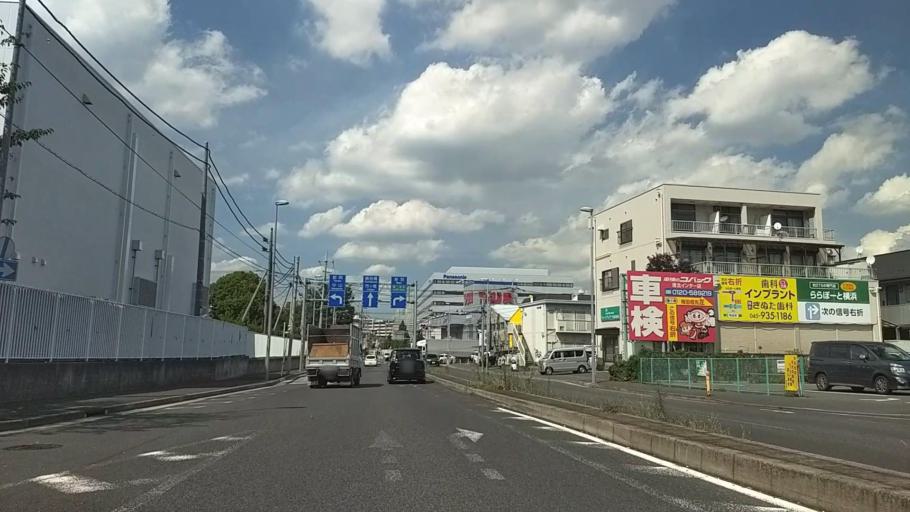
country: JP
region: Kanagawa
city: Yokohama
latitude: 35.5140
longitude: 139.5640
